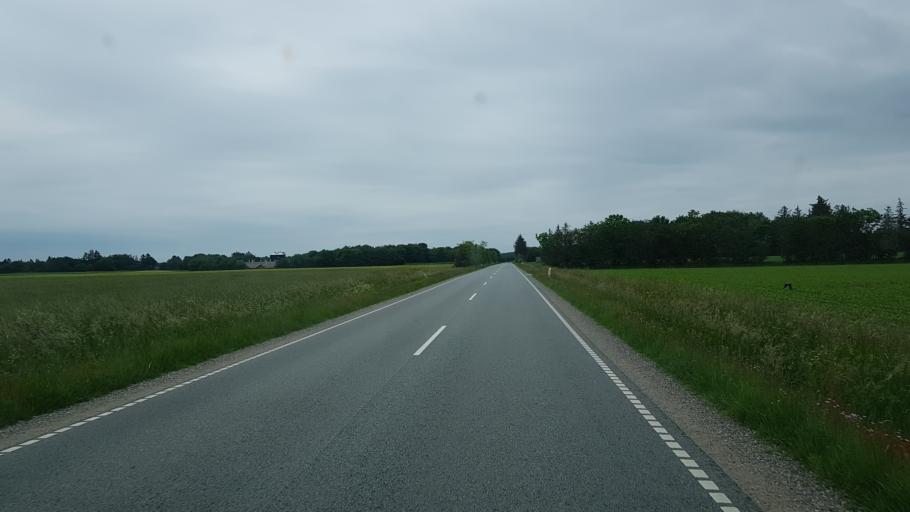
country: DK
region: South Denmark
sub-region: Varde Kommune
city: Olgod
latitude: 55.7071
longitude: 8.6881
